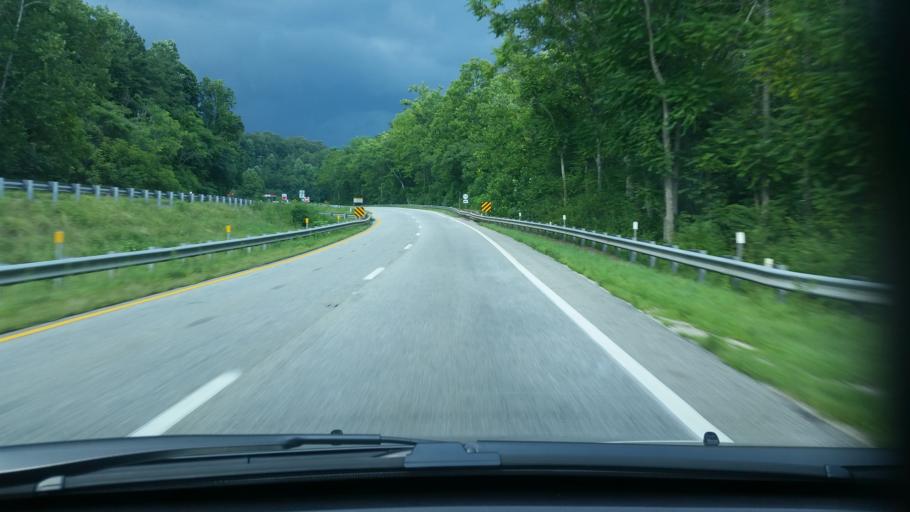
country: US
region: Virginia
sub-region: Nelson County
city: Nellysford
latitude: 37.8398
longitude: -78.8279
